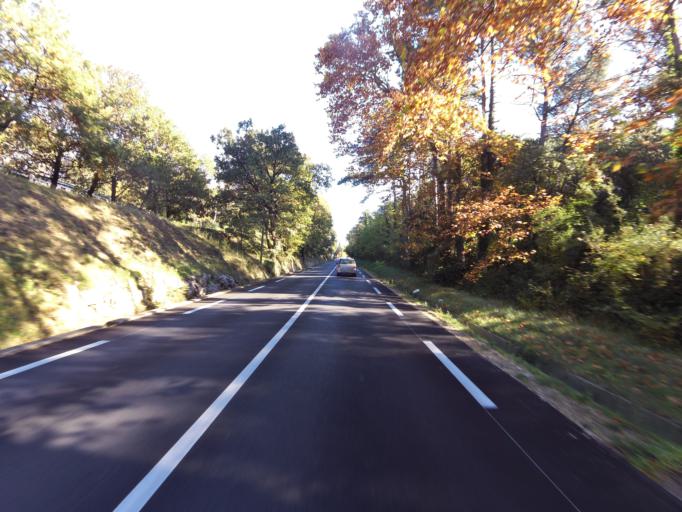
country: FR
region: Provence-Alpes-Cote d'Azur
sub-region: Departement du Vaucluse
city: Loriol-du-Comtat
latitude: 44.0714
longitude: 5.0083
